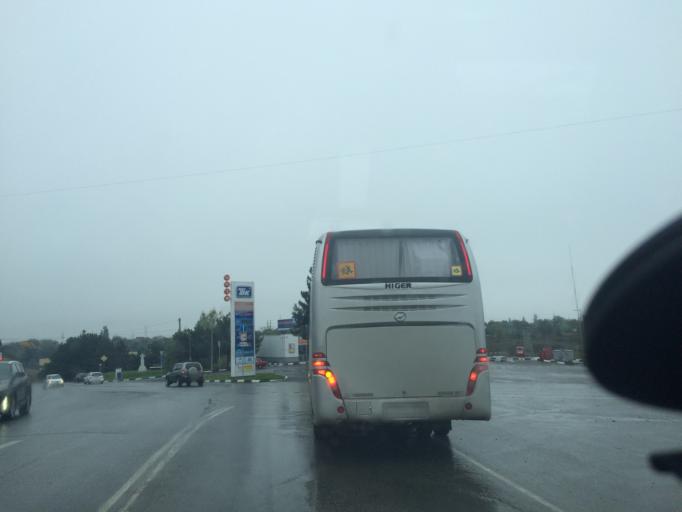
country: RU
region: Rostov
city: Azov
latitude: 47.0903
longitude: 39.4539
